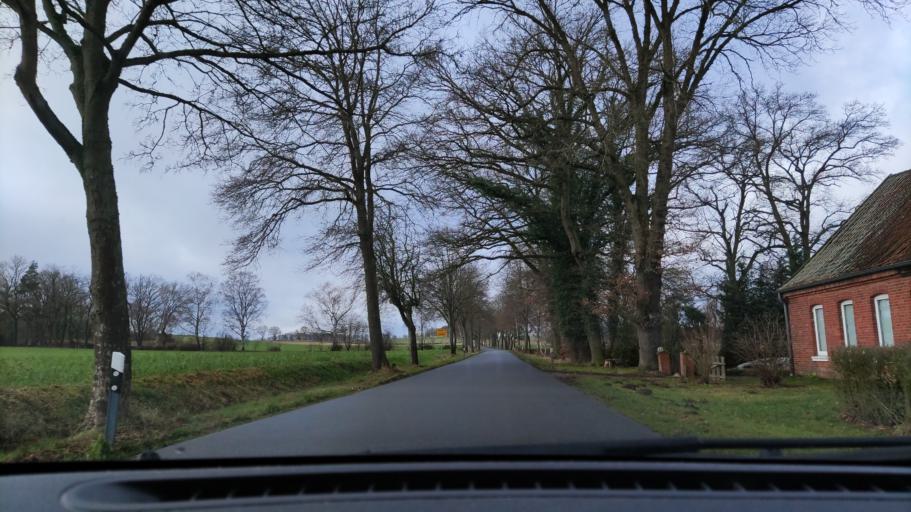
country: DE
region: Lower Saxony
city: Jelmstorf
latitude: 53.0799
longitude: 10.5093
